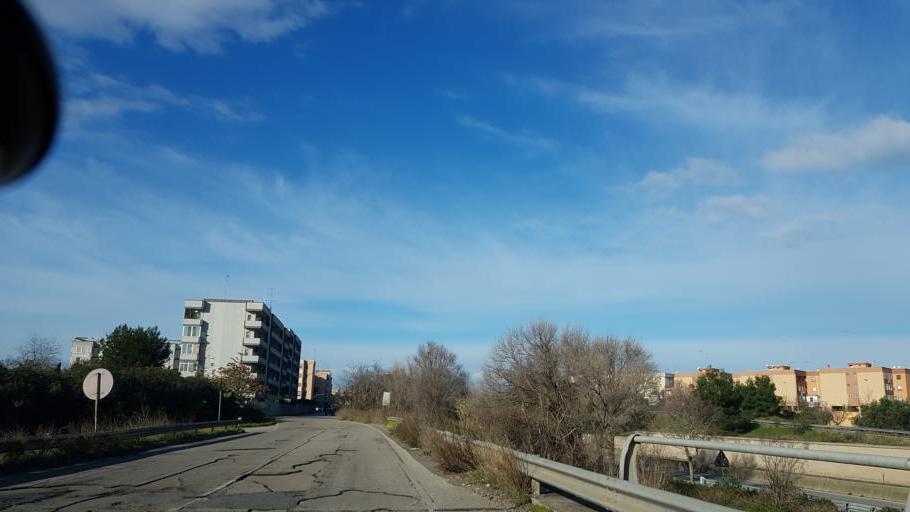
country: IT
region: Apulia
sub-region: Provincia di Brindisi
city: Brindisi
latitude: 40.6194
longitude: 17.9365
